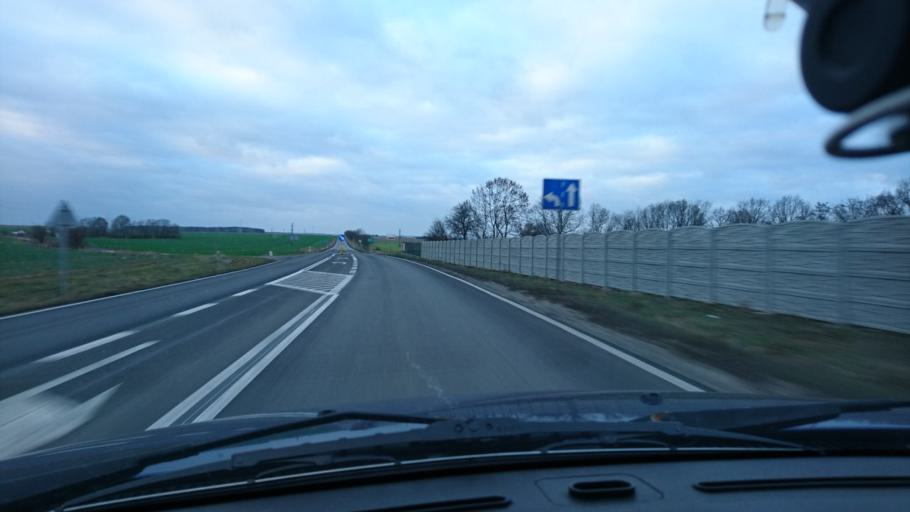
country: PL
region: Greater Poland Voivodeship
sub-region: Powiat kepinski
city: Slupia pod Kepnem
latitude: 51.2415
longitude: 18.0340
